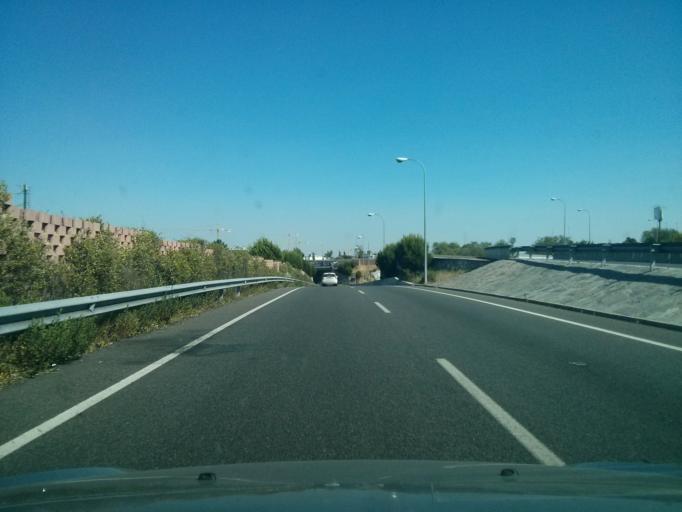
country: ES
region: Madrid
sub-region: Provincia de Madrid
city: Pozuelo de Alarcon
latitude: 40.4643
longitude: -3.8015
